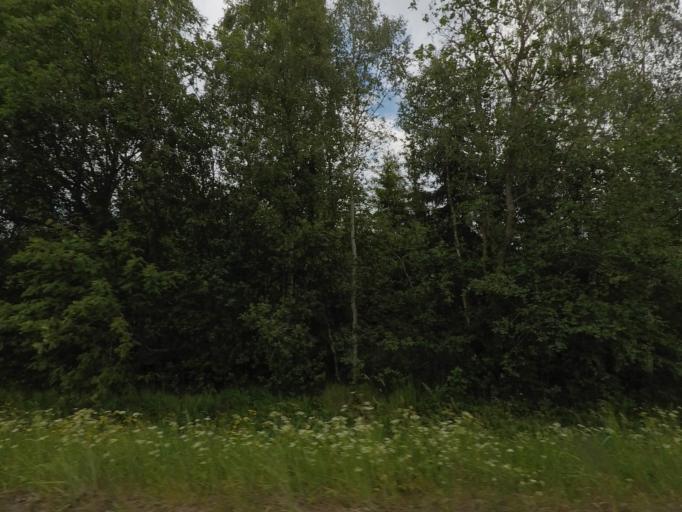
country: FI
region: Uusimaa
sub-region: Porvoo
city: Pukkila
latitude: 60.8108
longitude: 25.4815
